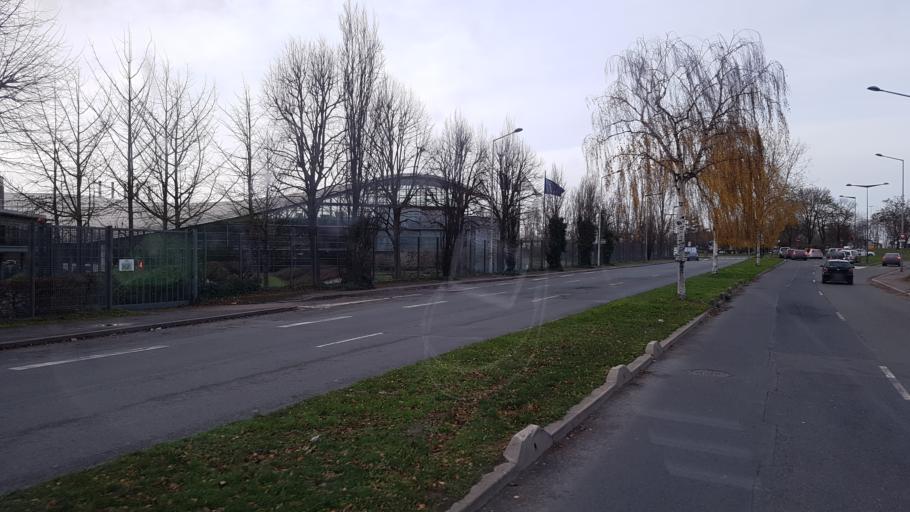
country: FR
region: Ile-de-France
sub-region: Departement de Seine-Saint-Denis
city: Aulnay-sous-Bois
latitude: 48.9503
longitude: 2.4876
